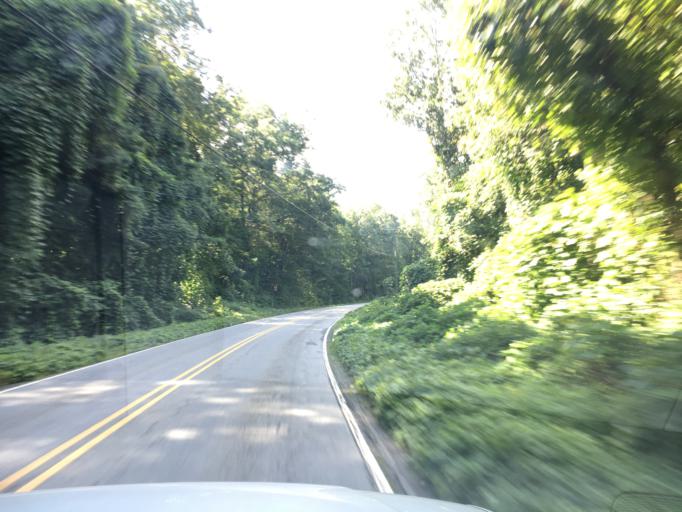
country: US
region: North Carolina
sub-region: Polk County
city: Columbus
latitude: 35.3216
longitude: -82.1818
